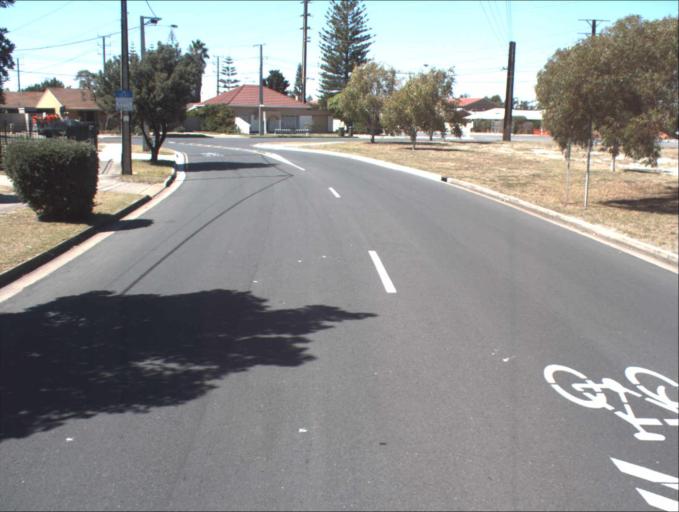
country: AU
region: South Australia
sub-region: Port Adelaide Enfield
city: Birkenhead
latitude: -34.8165
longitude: 138.5004
